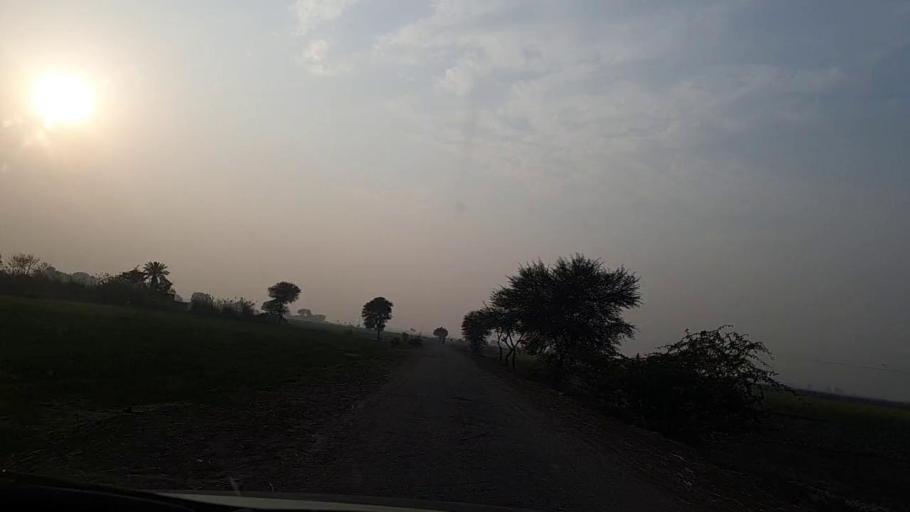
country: PK
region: Sindh
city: Nawabshah
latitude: 26.2979
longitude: 68.2690
